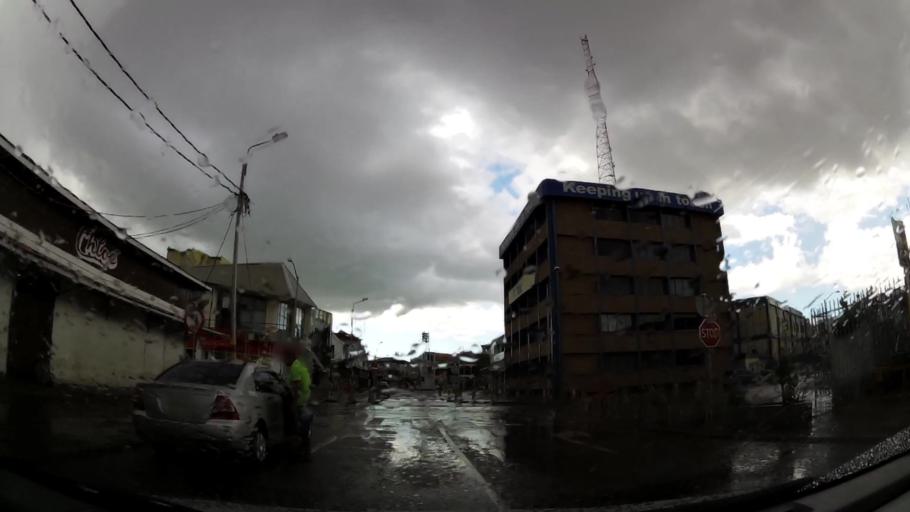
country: SR
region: Paramaribo
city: Paramaribo
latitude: 5.8256
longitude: -55.1571
